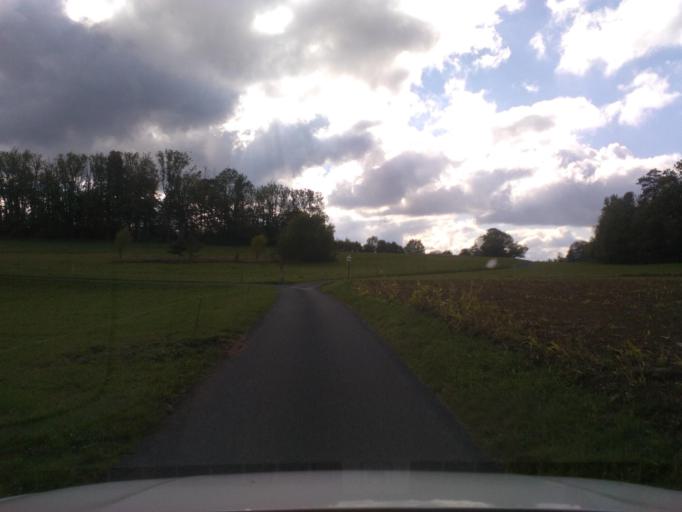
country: FR
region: Lorraine
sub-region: Departement des Vosges
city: Senones
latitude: 48.3504
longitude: 7.0187
